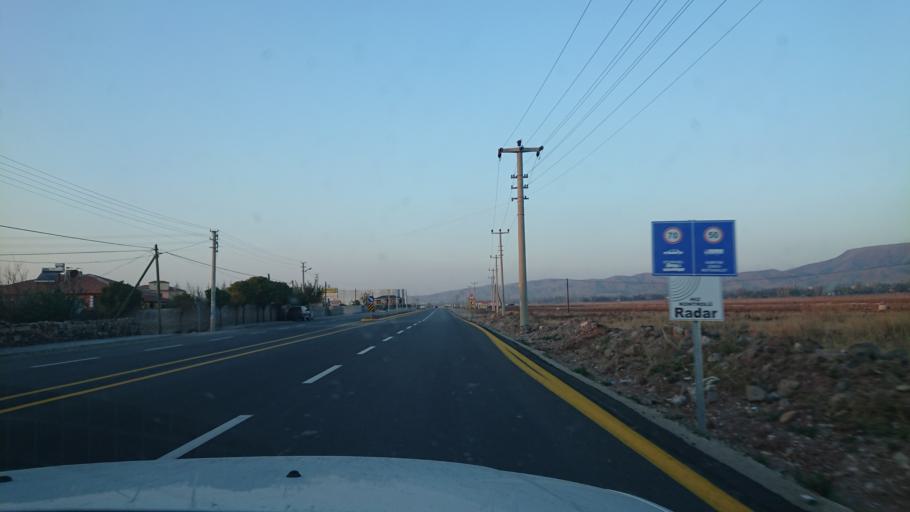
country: TR
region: Aksaray
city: Aksaray
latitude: 38.3194
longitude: 34.0531
